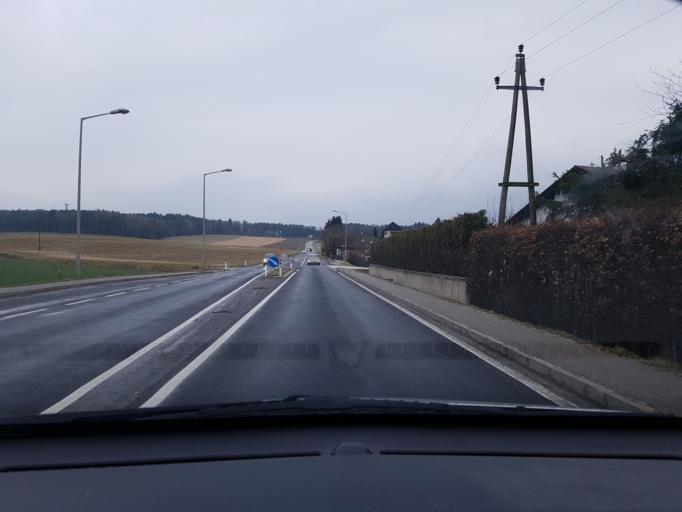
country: AT
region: Upper Austria
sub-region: Steyr Stadt
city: Steyr
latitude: 48.0706
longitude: 14.3828
